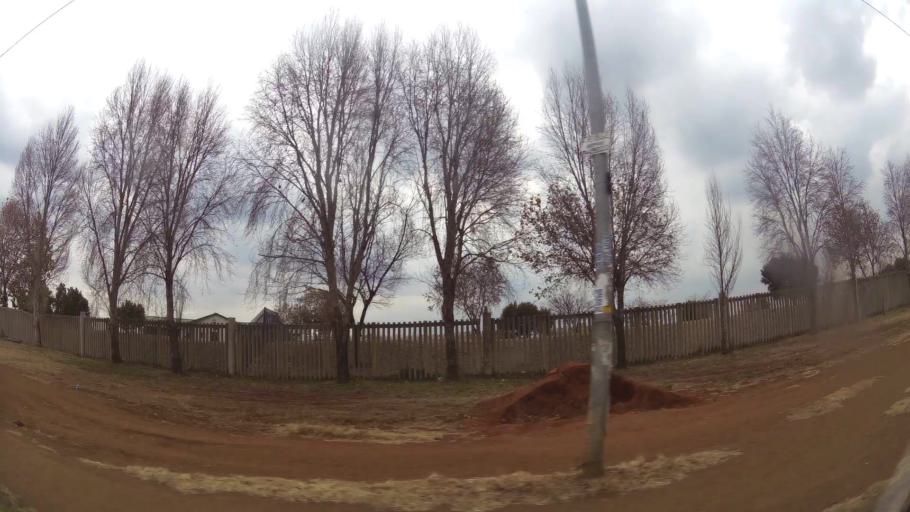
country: ZA
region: Gauteng
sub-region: Ekurhuleni Metropolitan Municipality
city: Germiston
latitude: -26.3786
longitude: 28.1486
